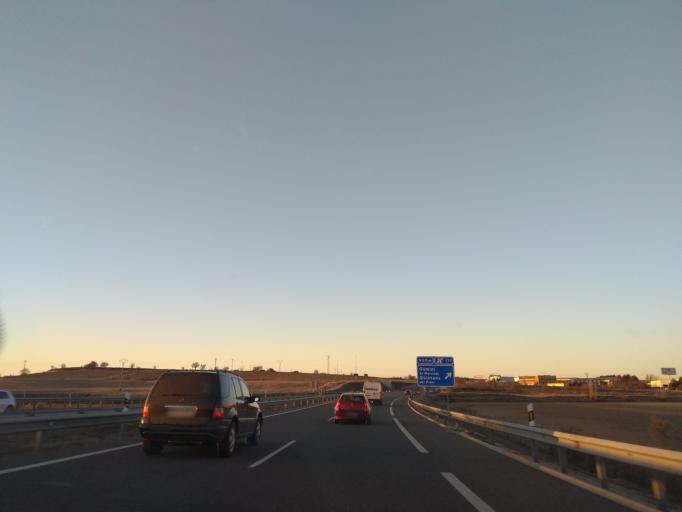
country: ES
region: Castille and Leon
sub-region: Provincia de Burgos
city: Quintana del Pidio
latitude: 41.7712
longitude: -3.6972
